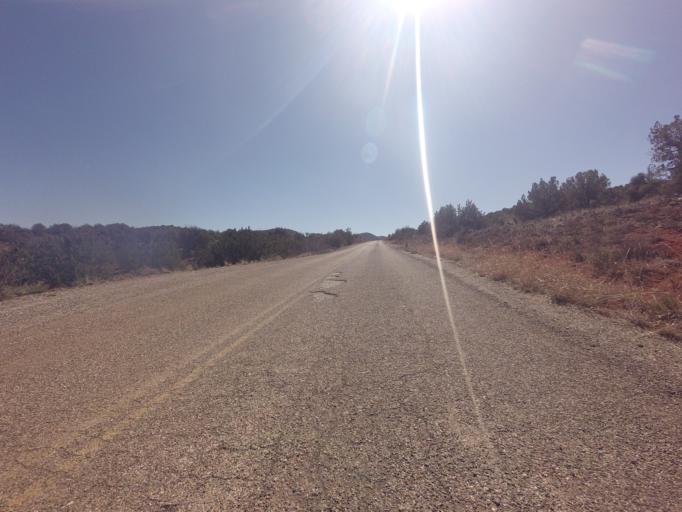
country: US
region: Arizona
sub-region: Yavapai County
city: Lake Montezuma
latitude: 34.6777
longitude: -111.7209
